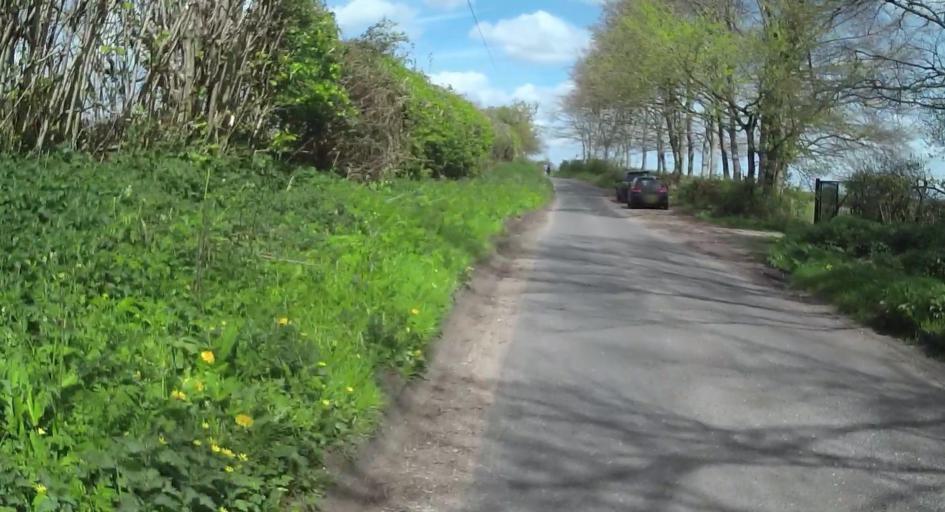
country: GB
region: England
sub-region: Hampshire
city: Romsey
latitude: 51.0435
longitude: -1.5383
